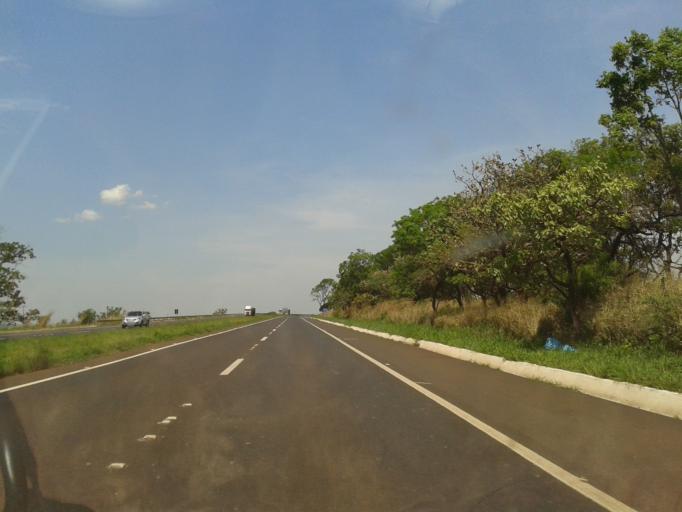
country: BR
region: Minas Gerais
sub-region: Monte Alegre De Minas
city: Monte Alegre de Minas
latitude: -18.8524
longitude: -48.7856
